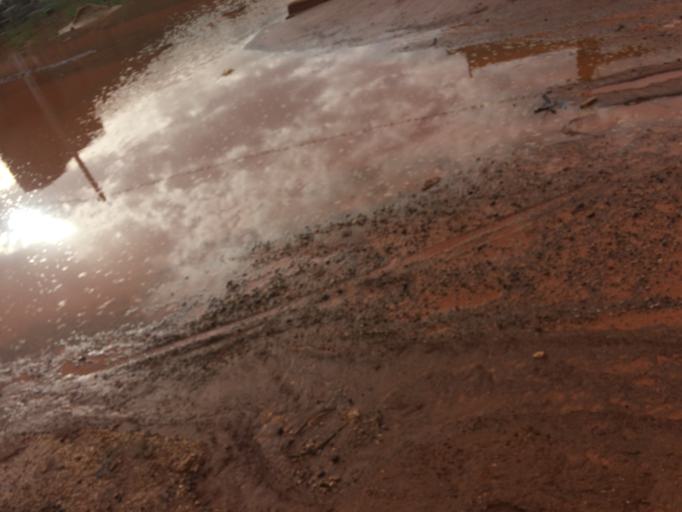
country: SN
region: Dakar
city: Pikine
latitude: 14.7427
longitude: -17.3052
